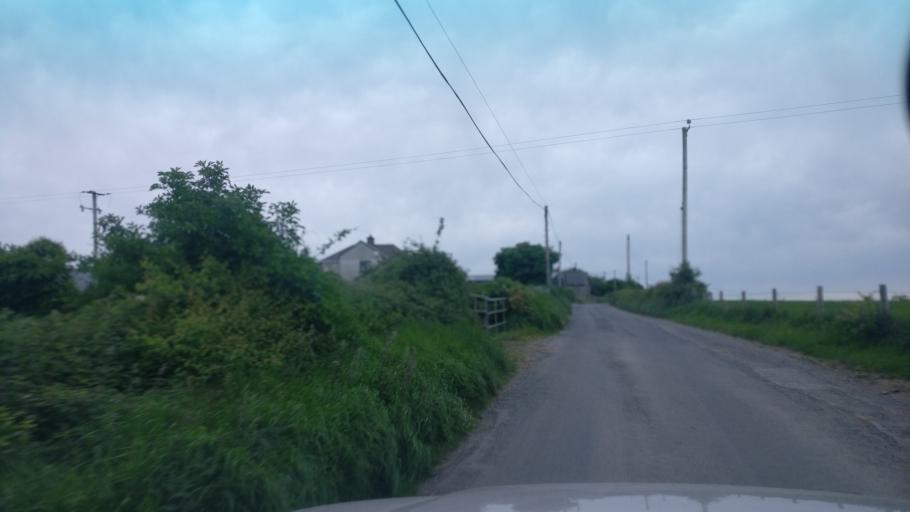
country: IE
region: Connaught
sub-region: County Galway
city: Portumna
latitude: 53.1458
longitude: -8.2885
